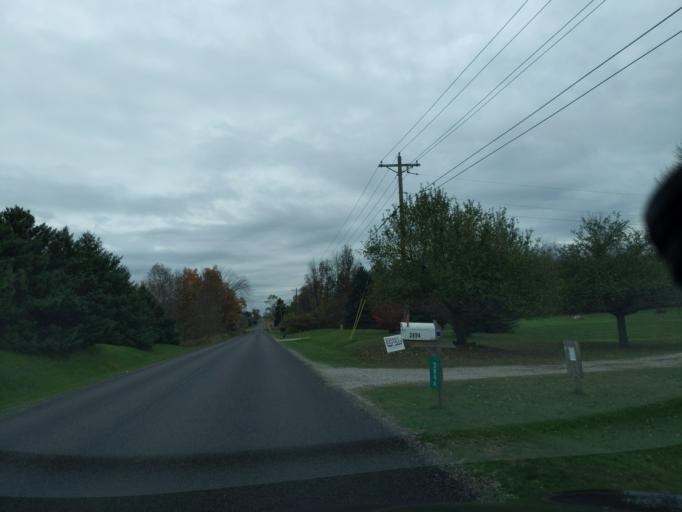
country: US
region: Michigan
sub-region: Eaton County
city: Eaton Rapids
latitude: 42.4689
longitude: -84.6008
